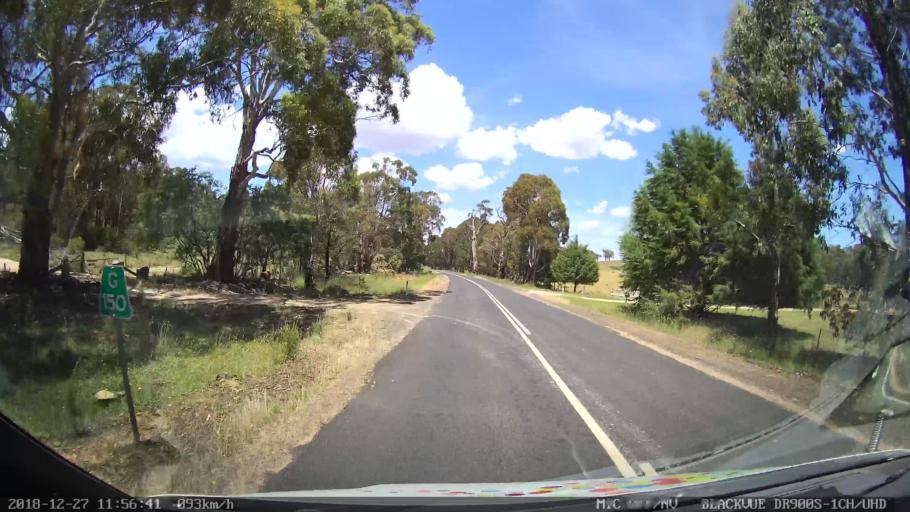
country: AU
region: New South Wales
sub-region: Blayney
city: Blayney
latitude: -33.7013
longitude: 149.3890
